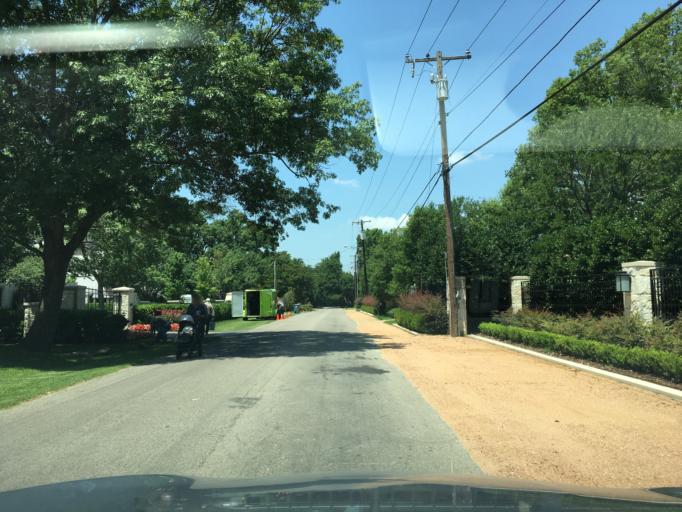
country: US
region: Texas
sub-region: Dallas County
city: University Park
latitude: 32.8726
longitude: -96.8062
